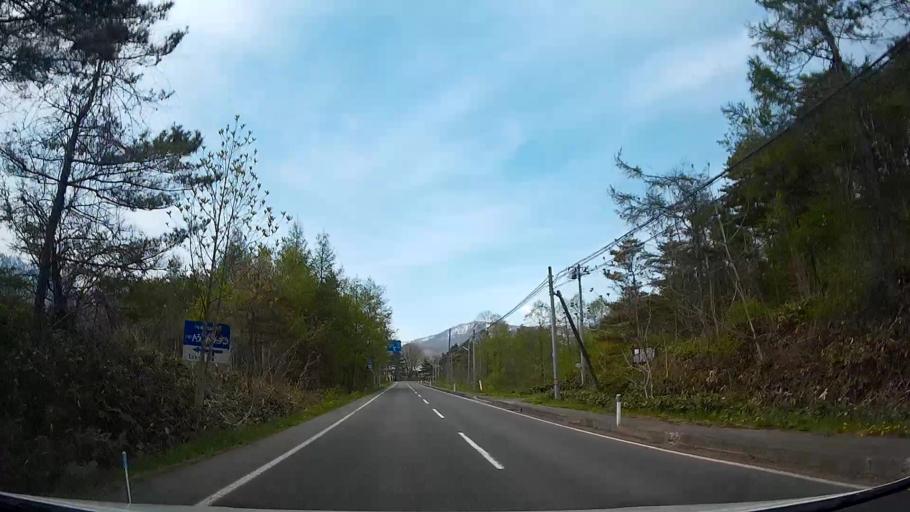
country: JP
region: Iwate
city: Shizukuishi
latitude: 39.9226
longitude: 140.9829
